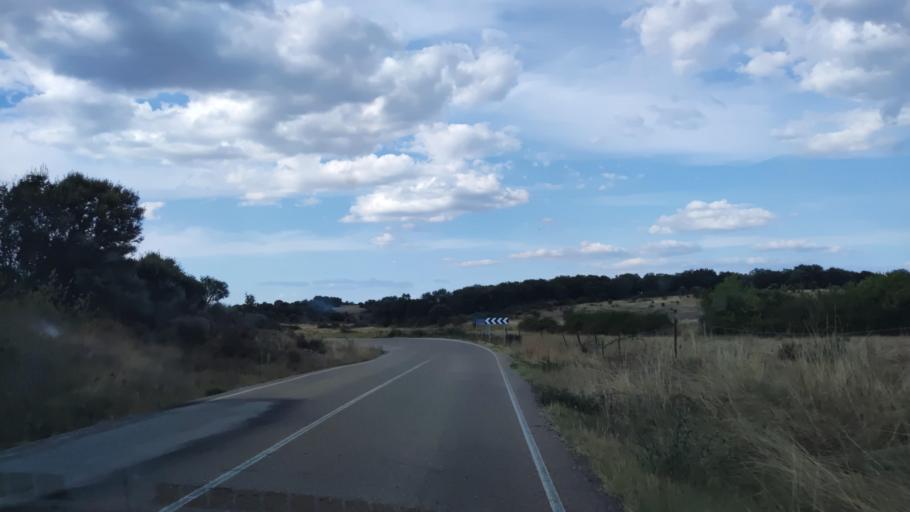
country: ES
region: Castille and Leon
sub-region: Provincia de Salamanca
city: Martiago
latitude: 40.4739
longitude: -6.4903
